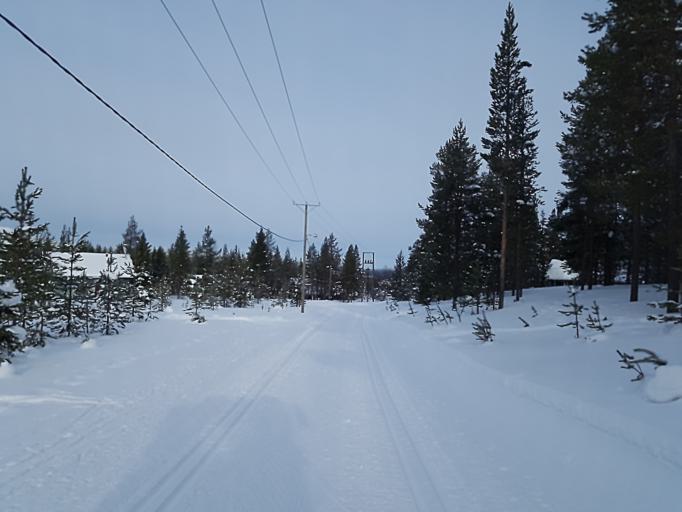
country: FI
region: Lapland
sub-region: Tunturi-Lappi
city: Kolari
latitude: 67.5959
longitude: 24.1596
